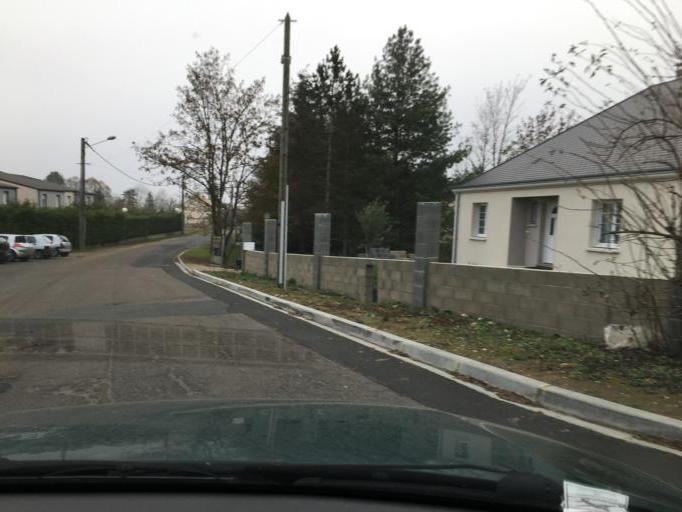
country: FR
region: Centre
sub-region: Departement du Loiret
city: Beaugency
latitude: 47.7850
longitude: 1.6376
